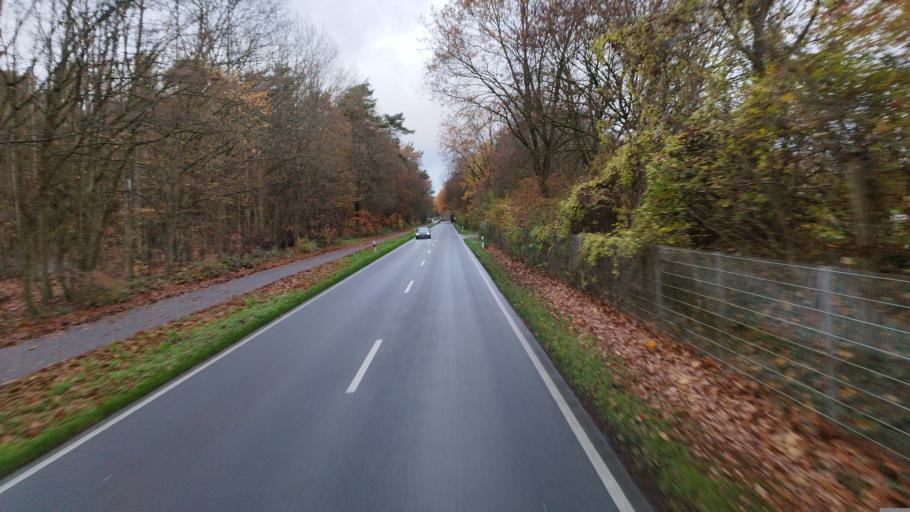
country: DE
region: Rheinland-Pfalz
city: Hatzenbuhl
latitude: 49.1339
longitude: 8.2192
